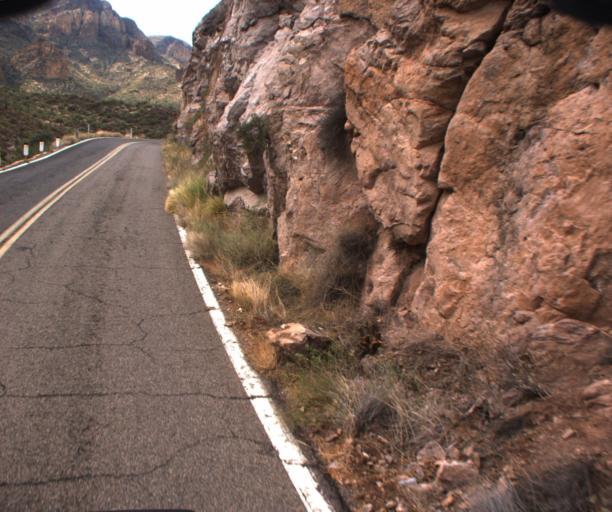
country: US
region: Arizona
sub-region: Pinal County
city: Apache Junction
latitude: 33.5331
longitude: -111.3786
